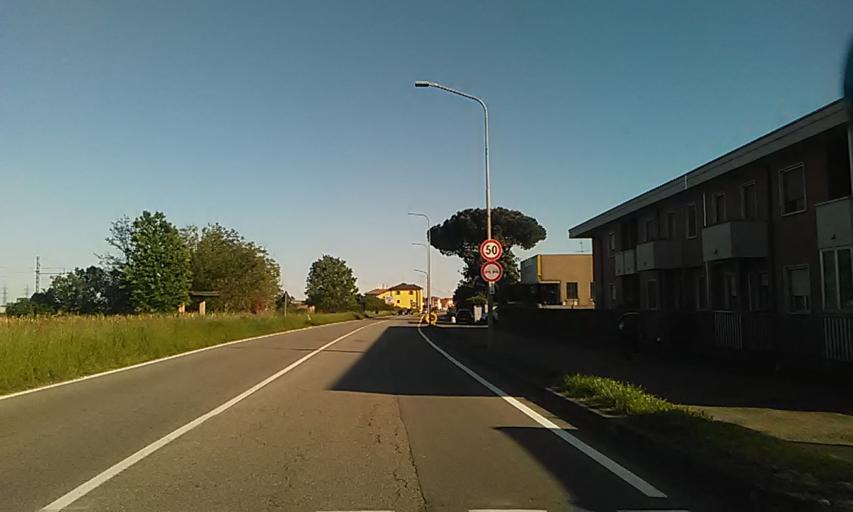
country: IT
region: Piedmont
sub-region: Provincia di Novara
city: Momo
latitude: 45.5824
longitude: 8.5499
